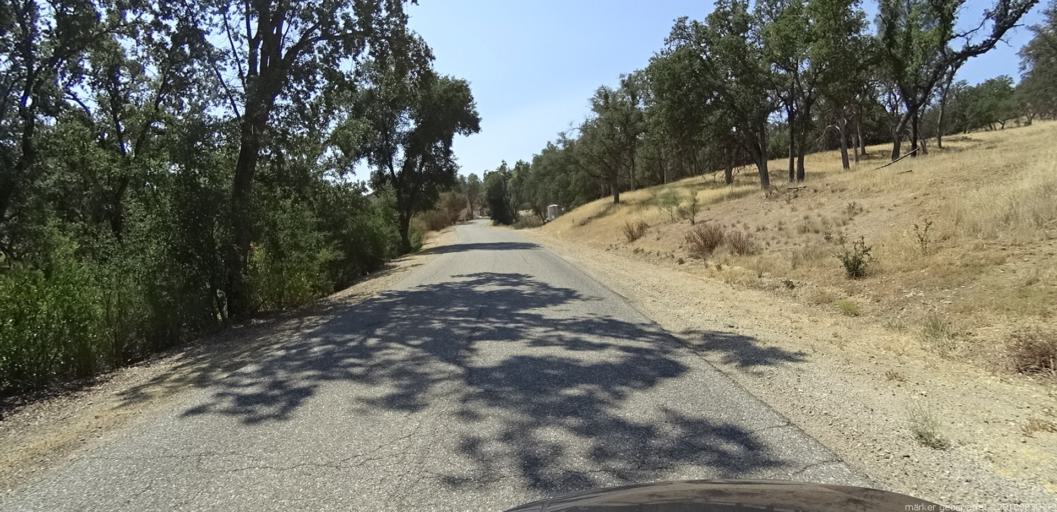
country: US
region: California
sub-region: Monterey County
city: King City
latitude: 35.9746
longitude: -121.2588
